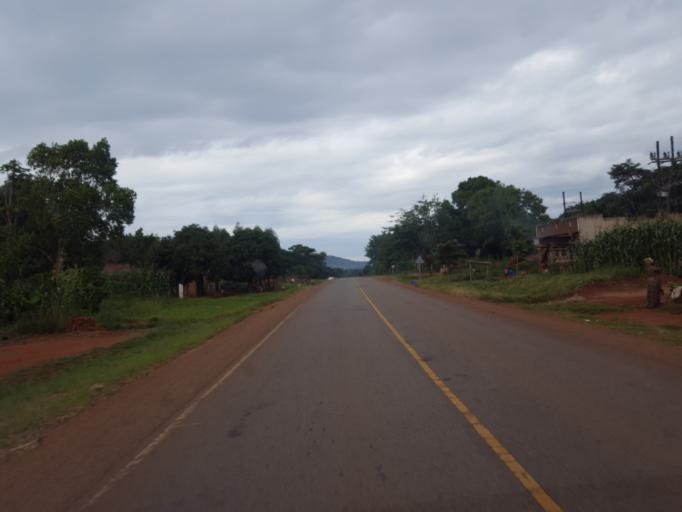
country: UG
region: Central Region
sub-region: Kiboga District
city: Kiboga
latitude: 1.0103
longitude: 31.6943
